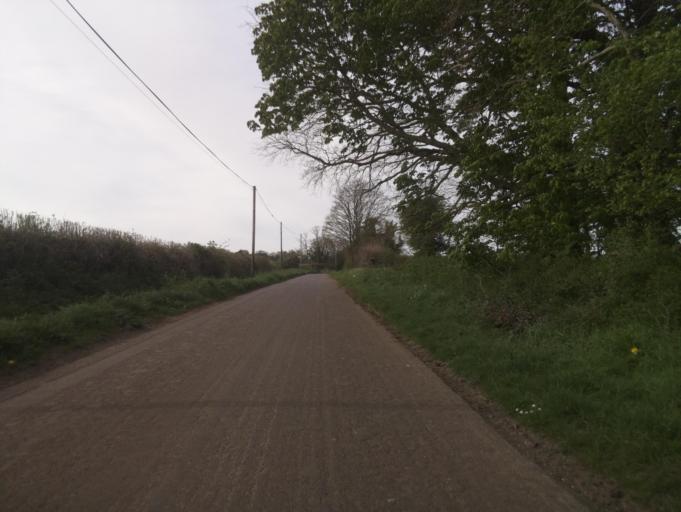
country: GB
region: England
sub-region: Somerset
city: Milborne Port
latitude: 50.9581
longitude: -2.4658
